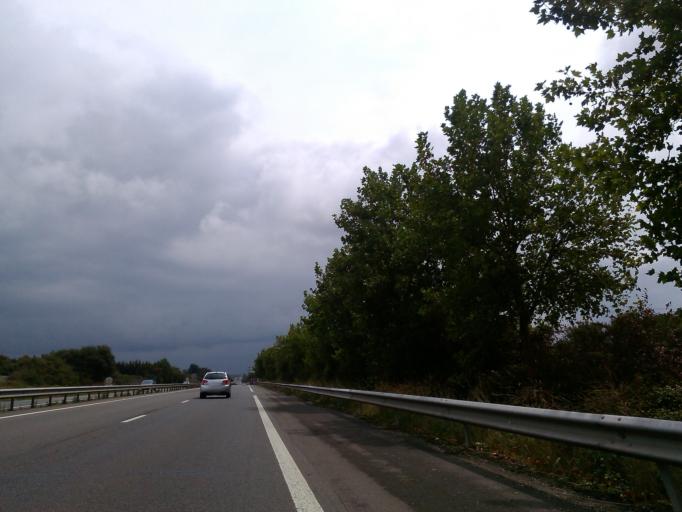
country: FR
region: Poitou-Charentes
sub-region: Departement de la Charente
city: Saint-Brice
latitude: 45.6782
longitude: -0.2812
